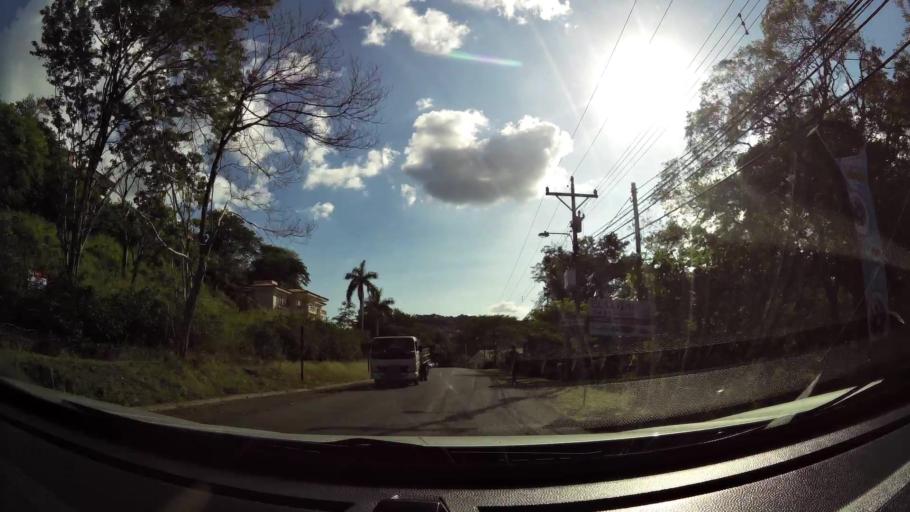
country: CR
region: Guanacaste
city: Sardinal
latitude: 10.5746
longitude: -85.6731
